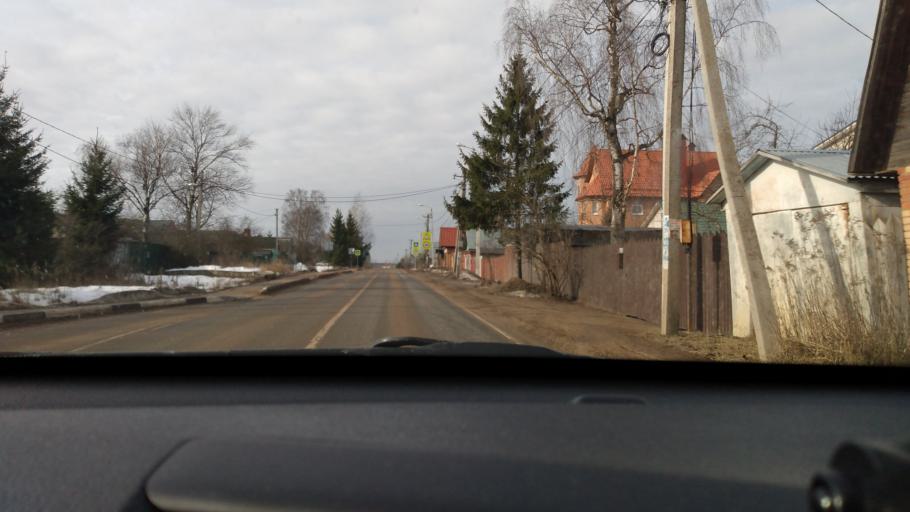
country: RU
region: Moskovskaya
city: Nakhabino
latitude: 55.8918
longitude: 37.1733
